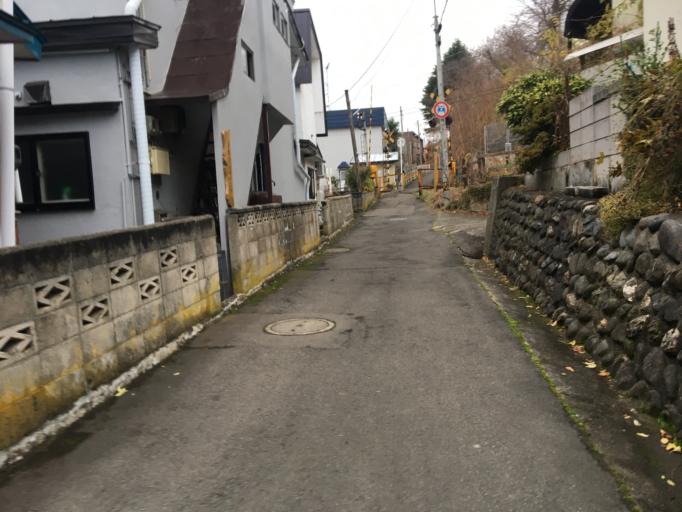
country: JP
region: Aomori
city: Hirosaki
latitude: 40.5945
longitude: 140.4687
